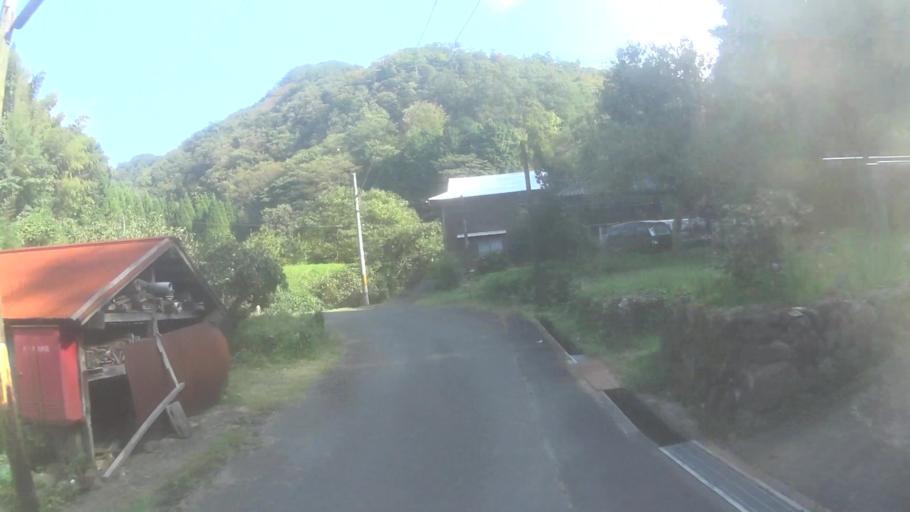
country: JP
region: Kyoto
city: Miyazu
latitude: 35.7138
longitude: 135.1289
